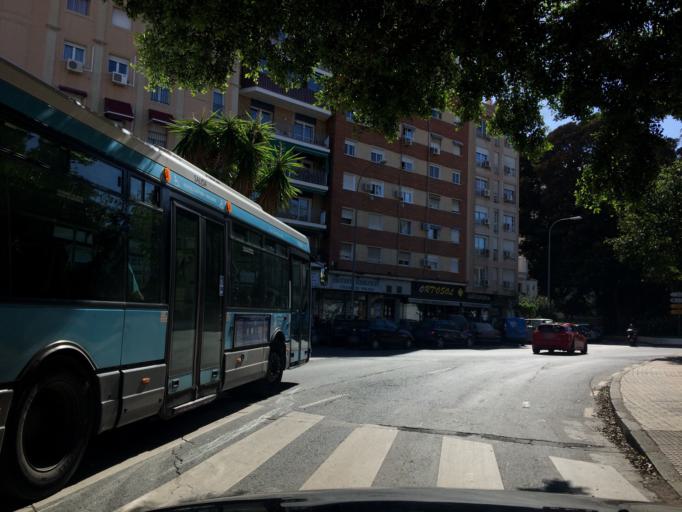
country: ES
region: Andalusia
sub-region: Provincia de Malaga
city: Malaga
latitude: 36.7281
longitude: -4.4304
